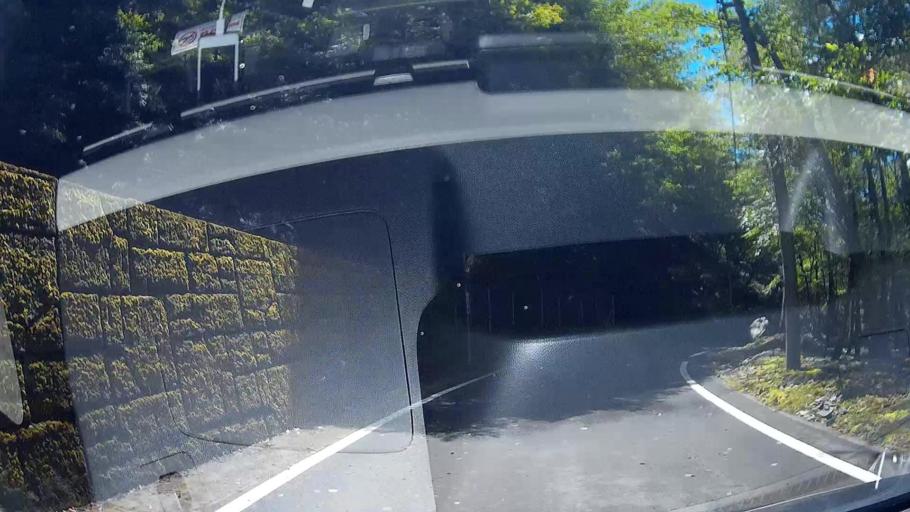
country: JP
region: Shizuoka
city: Fujinomiya
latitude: 35.3044
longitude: 138.3135
